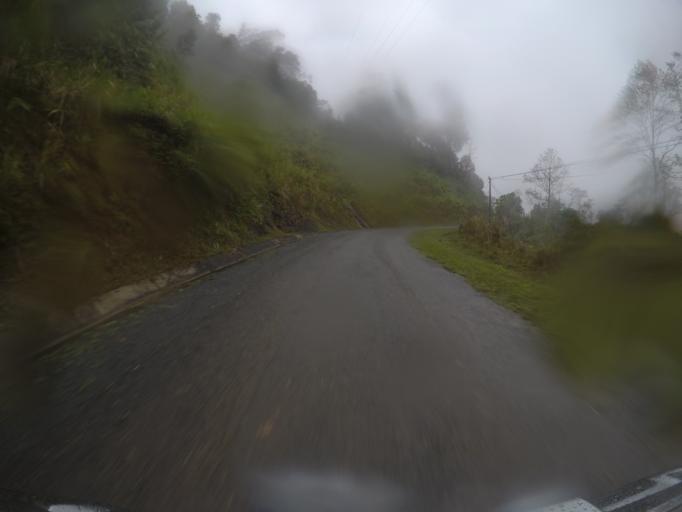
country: LA
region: Xekong
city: Dak Cheung
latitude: 15.5793
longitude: 107.4145
